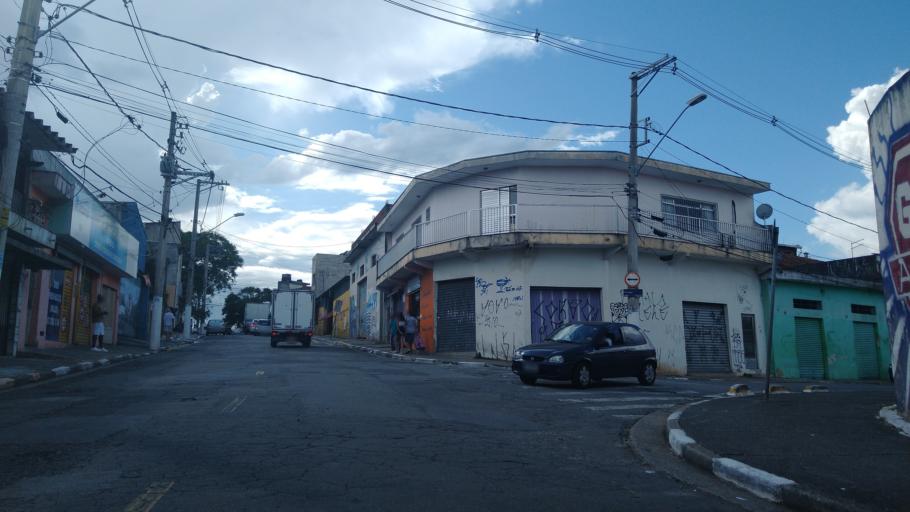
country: BR
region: Sao Paulo
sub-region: Osasco
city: Osasco
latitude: -23.5117
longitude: -46.7772
